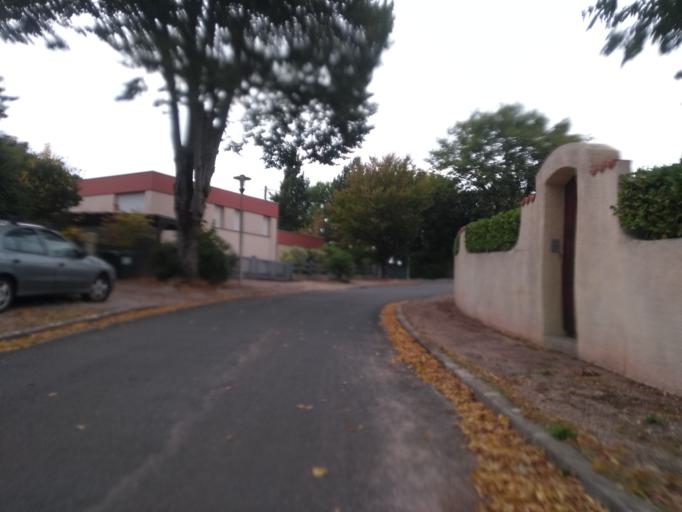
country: FR
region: Aquitaine
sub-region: Departement de la Gironde
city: Gradignan
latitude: 44.7798
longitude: -0.5988
